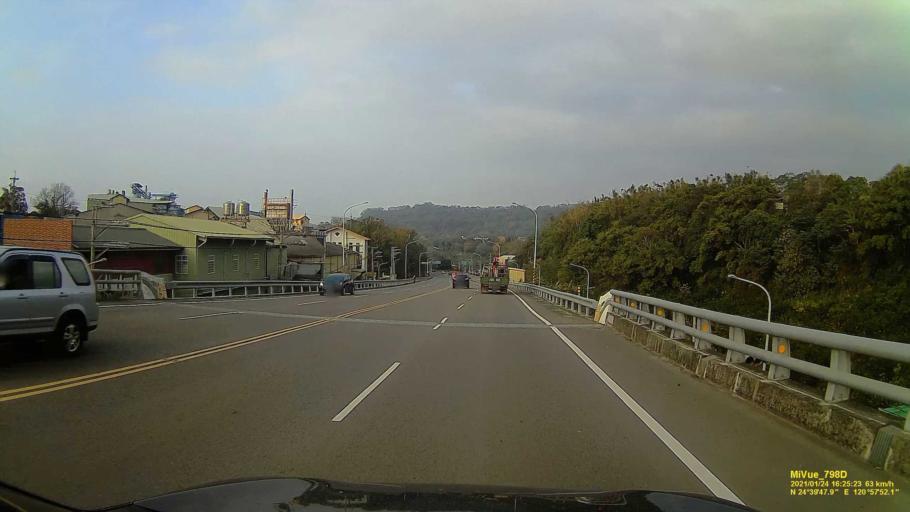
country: TW
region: Taiwan
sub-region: Hsinchu
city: Hsinchu
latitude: 24.6636
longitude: 120.9646
